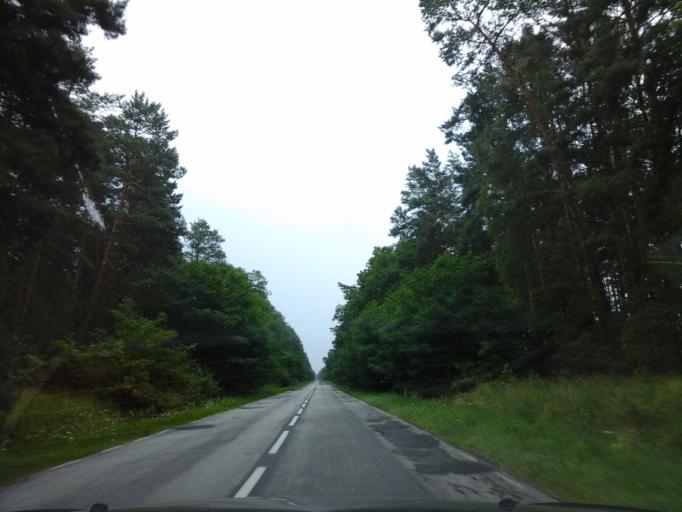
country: PL
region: Lubusz
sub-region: Powiat strzelecko-drezdenecki
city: Drezdenko
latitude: 52.7818
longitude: 15.8411
